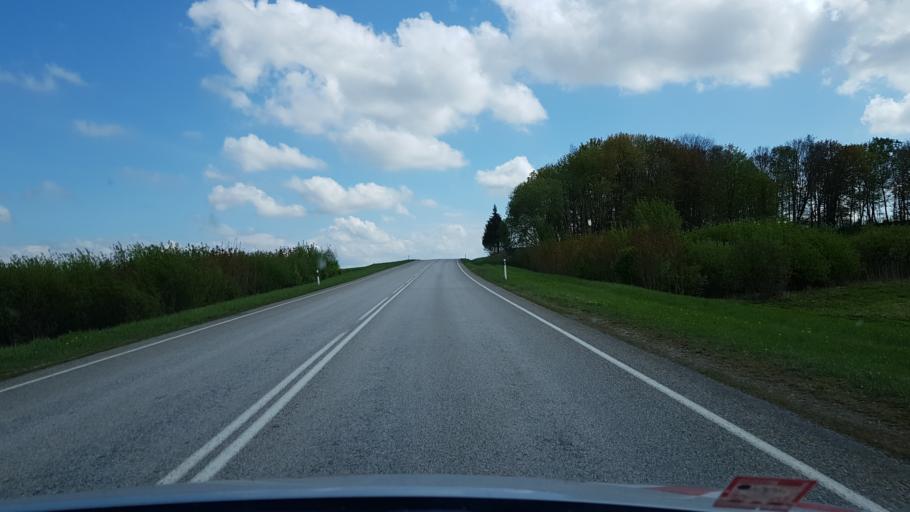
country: EE
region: Valgamaa
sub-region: Valga linn
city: Valga
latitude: 57.9051
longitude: 26.0466
